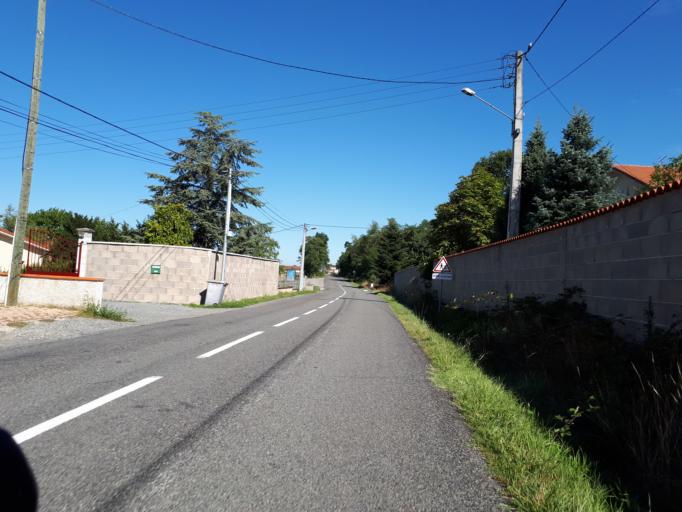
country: FR
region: Rhone-Alpes
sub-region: Departement de la Loire
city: Civens
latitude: 45.7729
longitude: 4.2592
